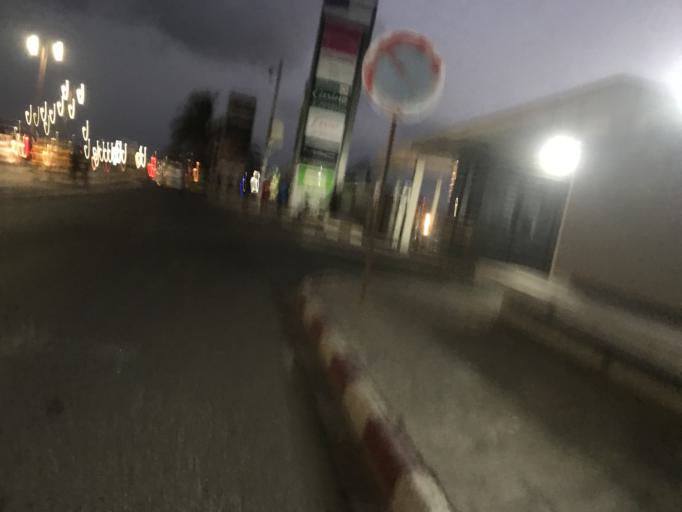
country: SN
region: Dakar
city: Mermoz Boabab
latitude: 14.6936
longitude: -17.4737
